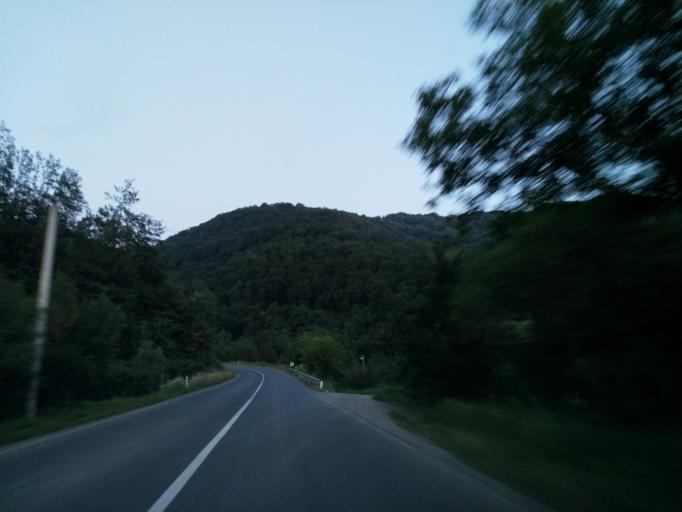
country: RS
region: Central Serbia
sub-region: Rasinski Okrug
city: Aleksandrovac
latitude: 43.3437
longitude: 21.0923
